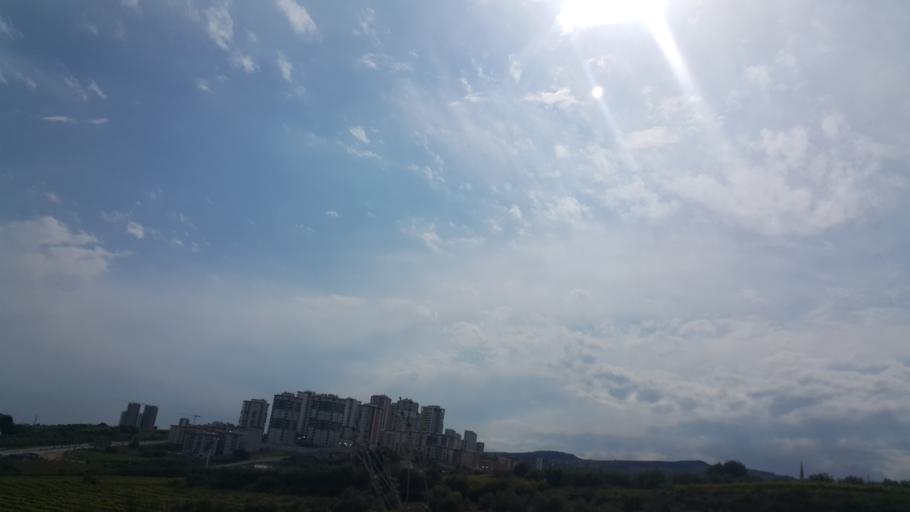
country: TR
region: Mersin
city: Tarsus
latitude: 36.9453
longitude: 34.8609
